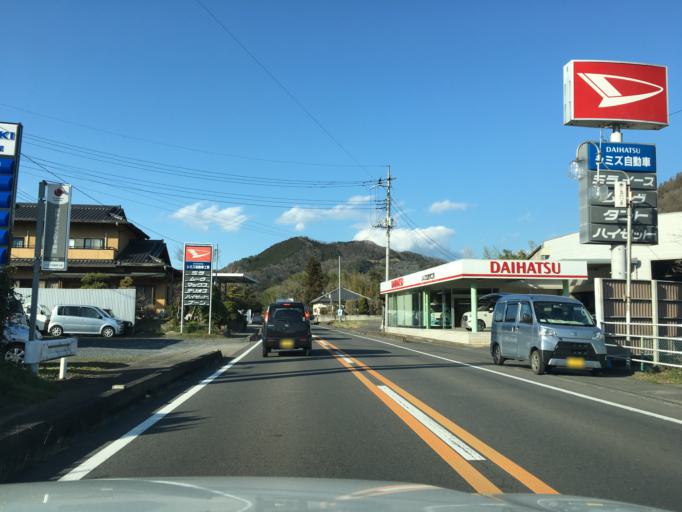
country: JP
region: Ibaraki
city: Omiya
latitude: 36.6480
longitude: 140.3933
